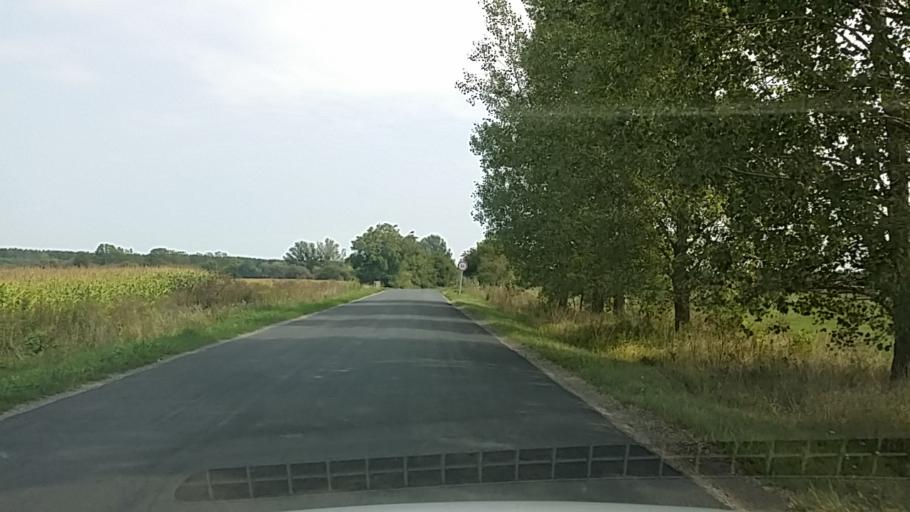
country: HU
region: Gyor-Moson-Sopron
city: Bosarkany
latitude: 47.7198
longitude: 17.2949
